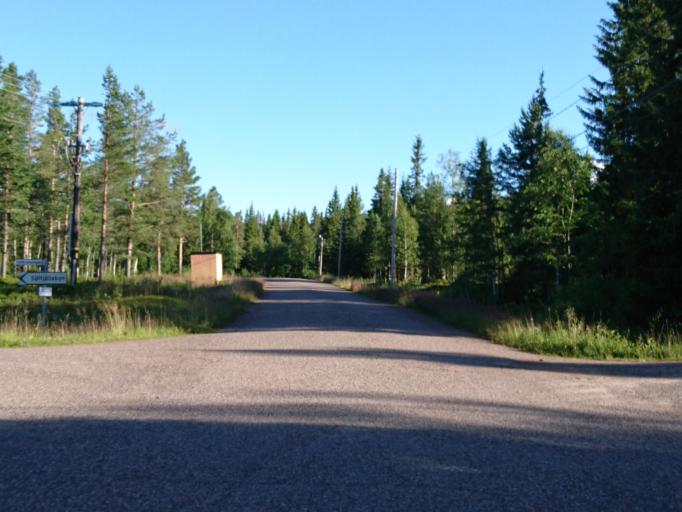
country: SE
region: Dalarna
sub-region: Malung-Saelens kommun
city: Malung
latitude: 61.1718
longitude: 13.1761
